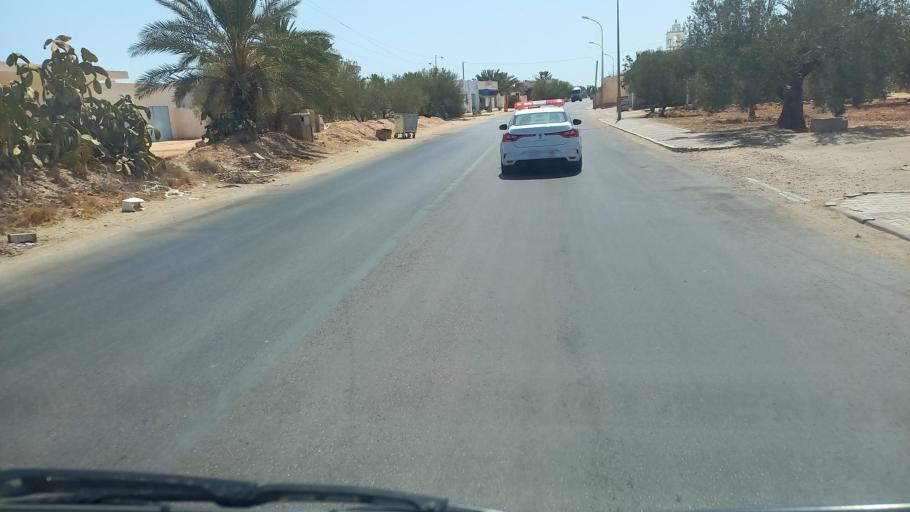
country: TN
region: Madanin
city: Midoun
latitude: 33.7701
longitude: 10.8999
